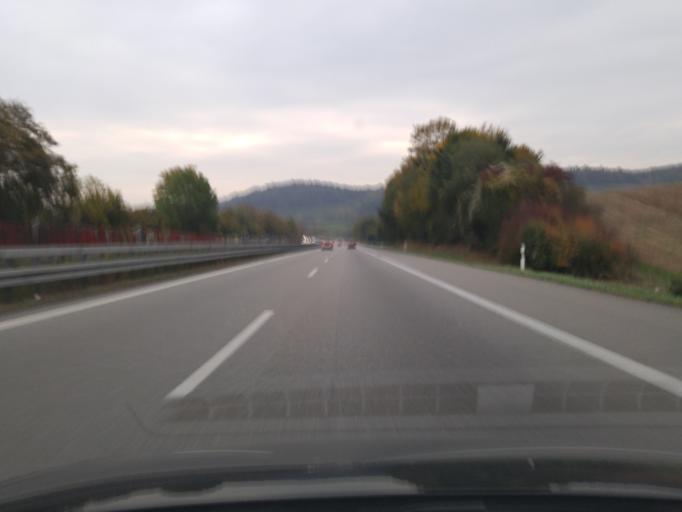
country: DE
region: Baden-Wuerttemberg
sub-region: Regierungsbezirk Stuttgart
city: Ellhofen
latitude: 49.1612
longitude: 9.3412
